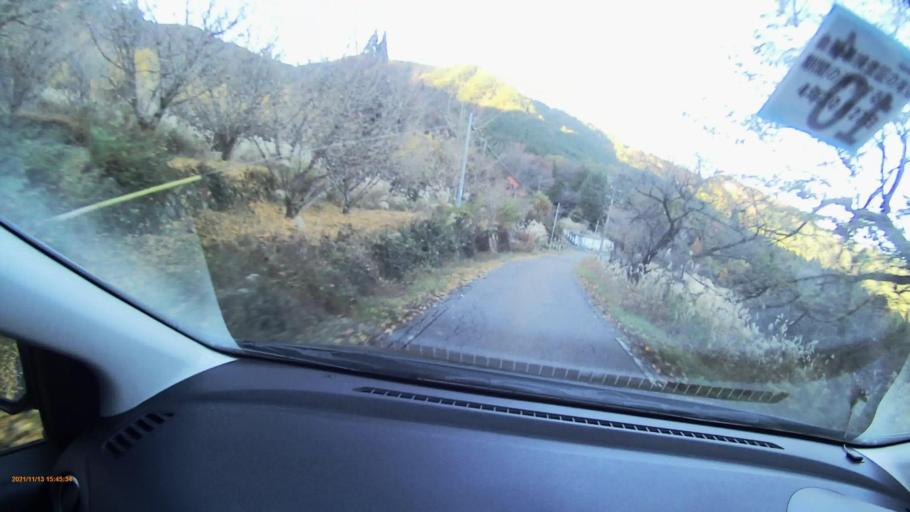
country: JP
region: Gifu
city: Nakatsugawa
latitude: 35.5945
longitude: 137.3973
